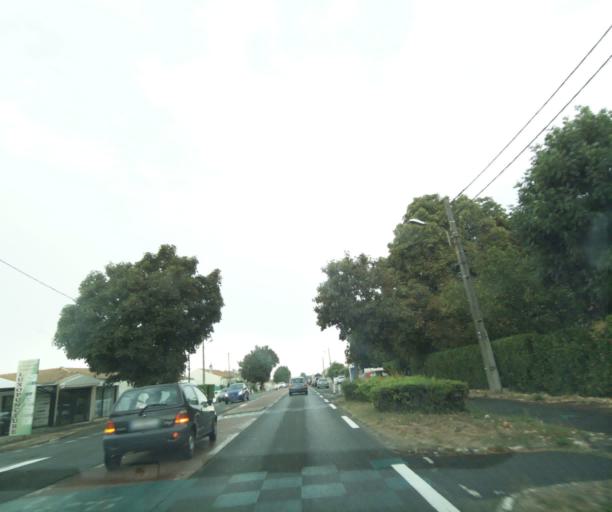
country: FR
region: Poitou-Charentes
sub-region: Departement de la Charente-Maritime
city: Tonnay-Charente
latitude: 45.9484
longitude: -0.9144
